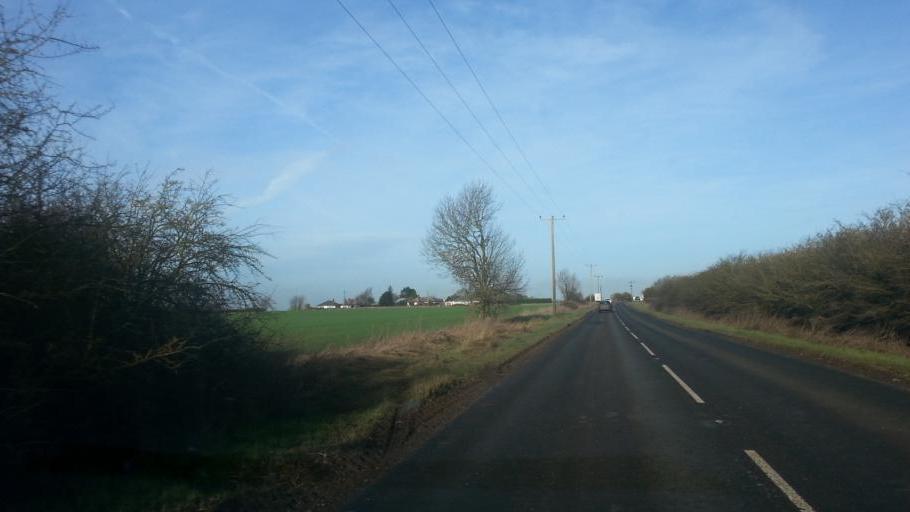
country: GB
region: England
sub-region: Cambridgeshire
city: Warboys
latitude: 52.4132
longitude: -0.1044
